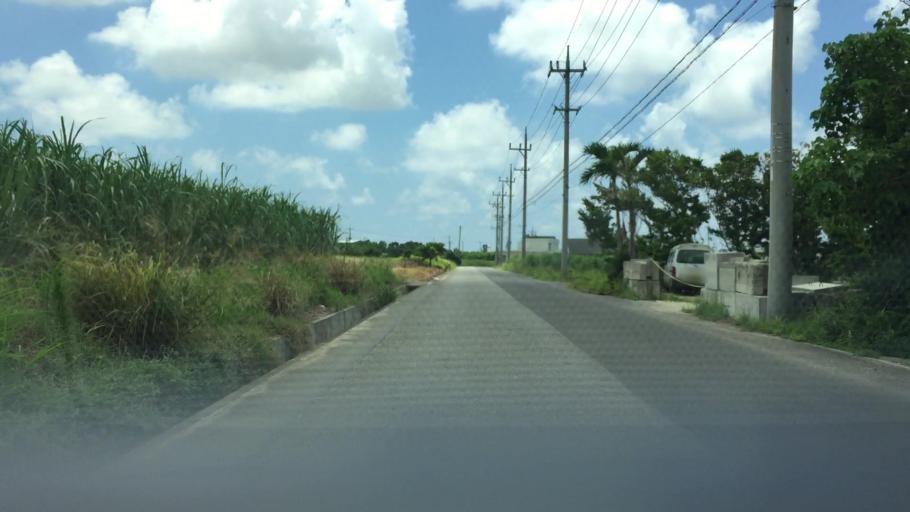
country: JP
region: Okinawa
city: Ishigaki
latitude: 24.3588
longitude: 124.1418
